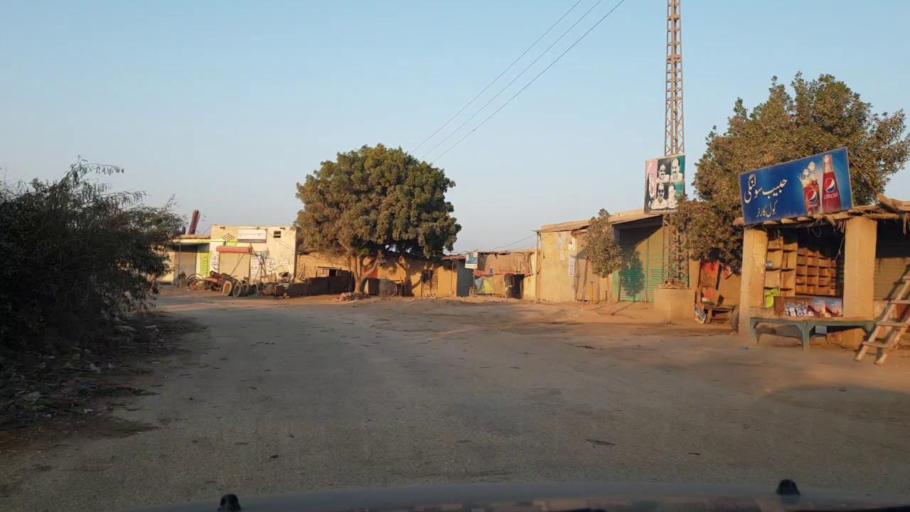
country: PK
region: Sindh
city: Chambar
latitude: 25.2625
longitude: 68.6598
